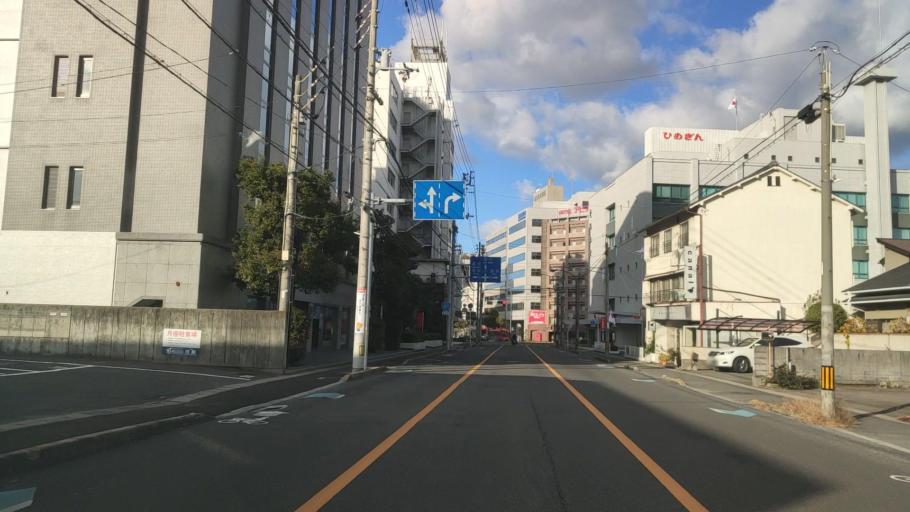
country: JP
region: Ehime
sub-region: Shikoku-chuo Shi
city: Matsuyama
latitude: 33.8416
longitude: 132.7767
